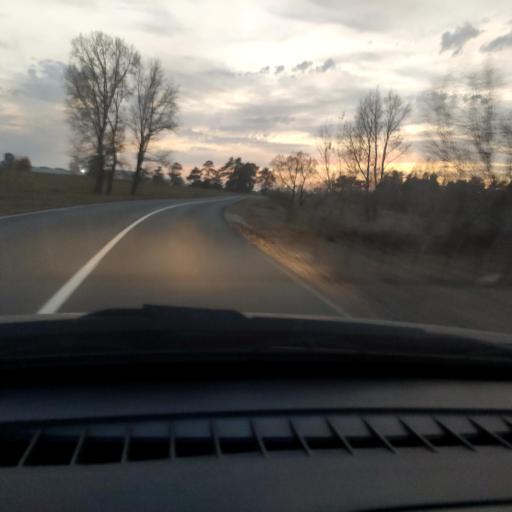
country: RU
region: Samara
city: Povolzhskiy
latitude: 53.5538
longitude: 49.6274
